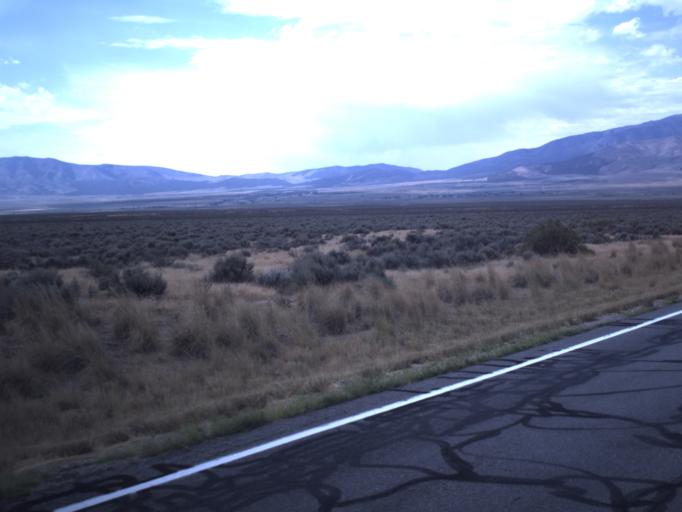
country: US
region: Utah
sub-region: Tooele County
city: Tooele
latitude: 40.3654
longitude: -112.3419
